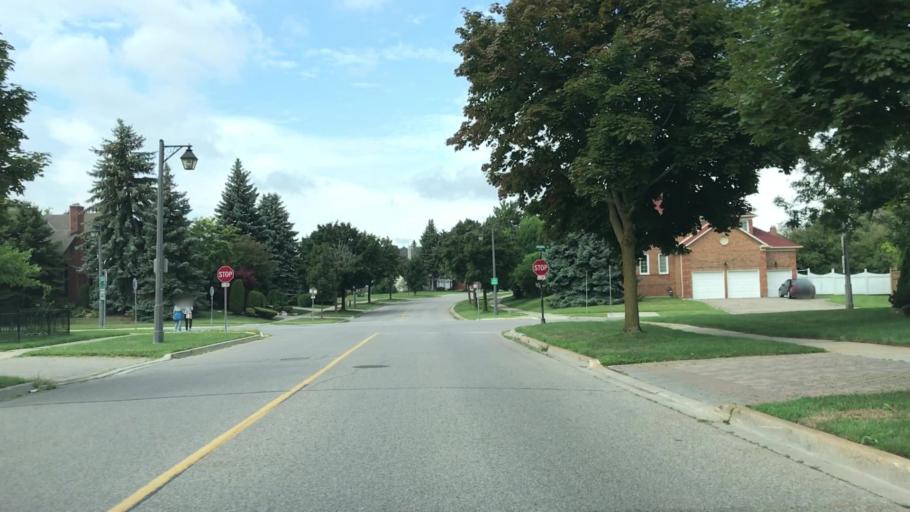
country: CA
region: Ontario
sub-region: York
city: Richmond Hill
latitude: 43.8643
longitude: -79.3985
